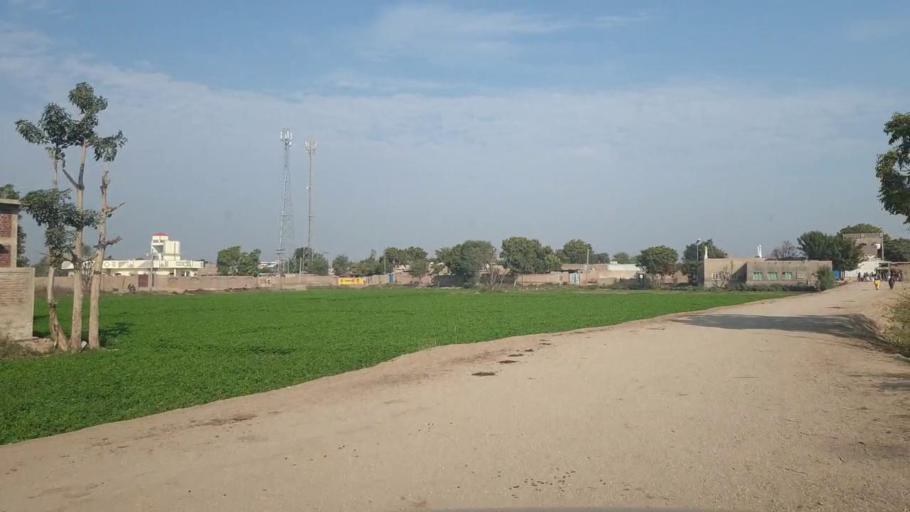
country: PK
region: Sindh
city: Tando Adam
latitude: 25.7533
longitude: 68.5962
